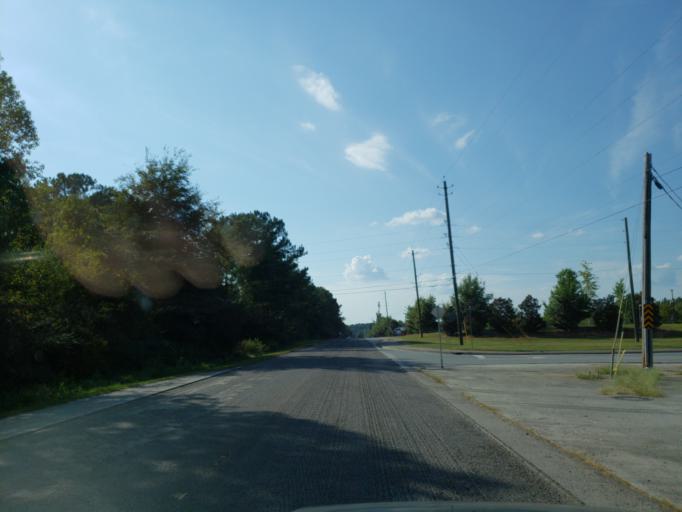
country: US
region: Georgia
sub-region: Cobb County
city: Powder Springs
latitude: 33.8661
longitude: -84.6996
